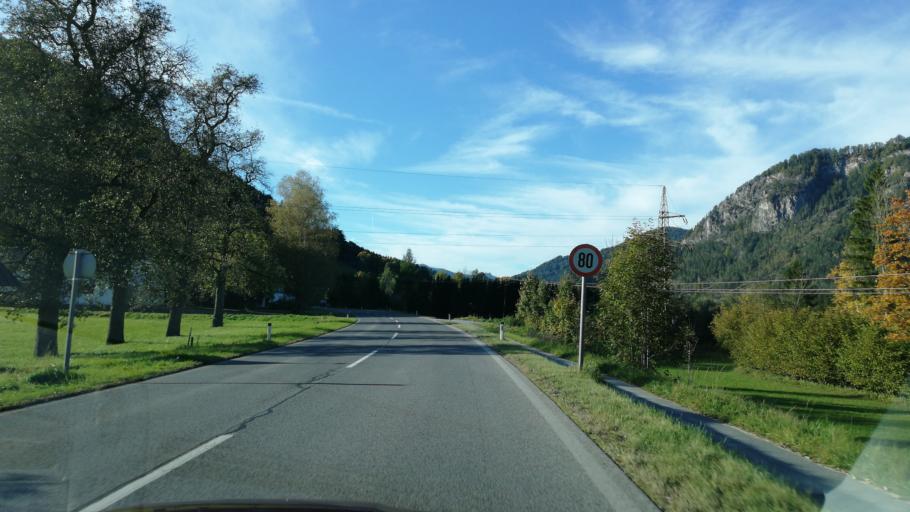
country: AT
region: Styria
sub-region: Politischer Bezirk Liezen
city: Landl
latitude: 47.6480
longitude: 14.7521
